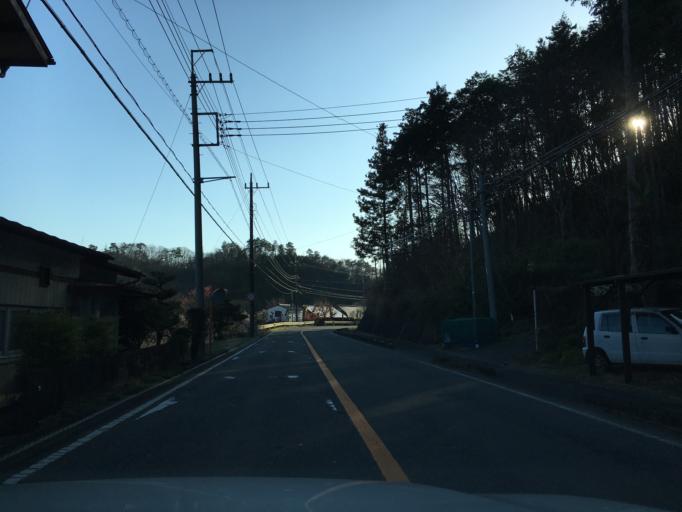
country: JP
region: Ibaraki
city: Daigo
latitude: 36.7657
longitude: 140.2300
